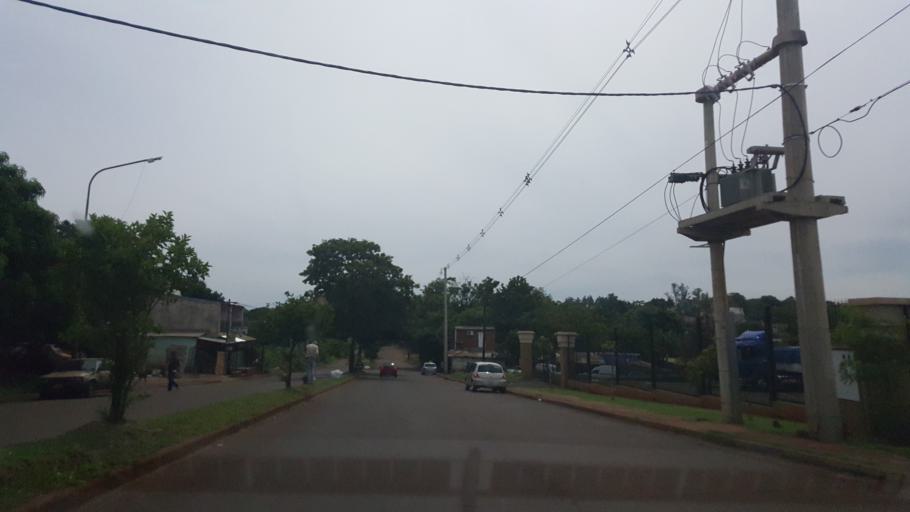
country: AR
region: Misiones
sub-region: Departamento de Capital
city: Posadas
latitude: -27.3908
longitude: -55.9426
